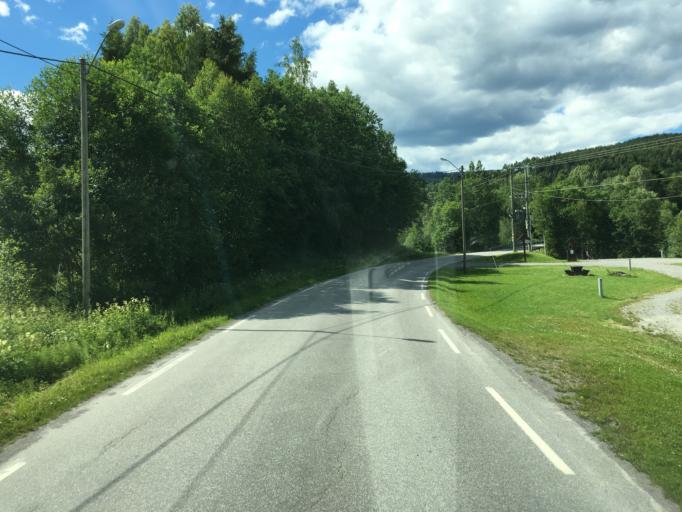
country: NO
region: Oppland
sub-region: Sondre Land
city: Hov
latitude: 60.5198
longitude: 10.2862
